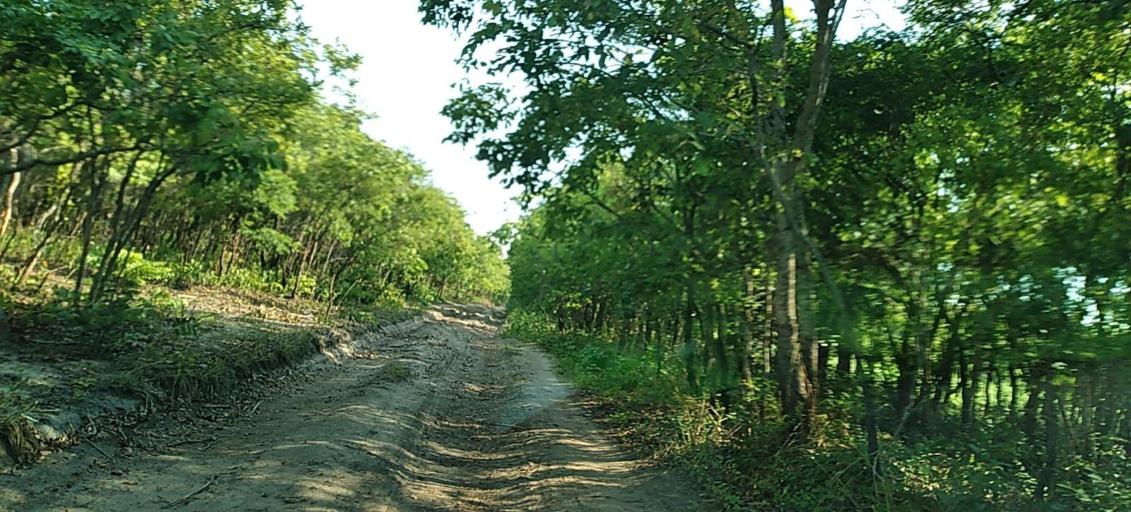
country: ZM
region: North-Western
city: Mwinilunga
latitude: -11.3197
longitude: 24.7393
